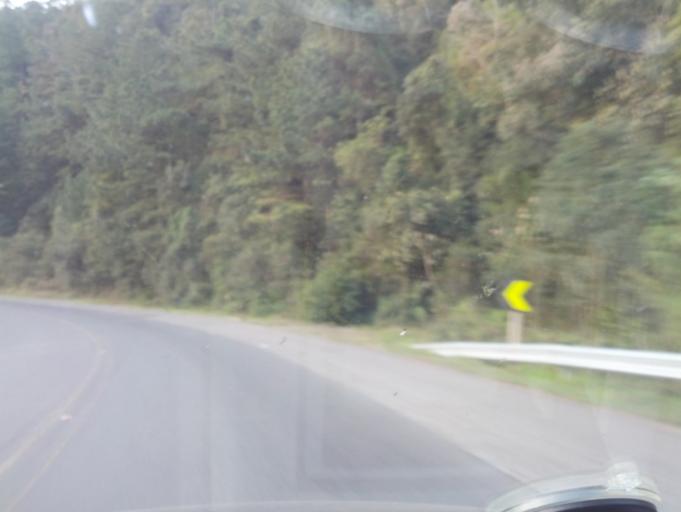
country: BR
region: Santa Catarina
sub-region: Otacilio Costa
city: Otacilio Costa
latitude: -27.3020
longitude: -50.0754
